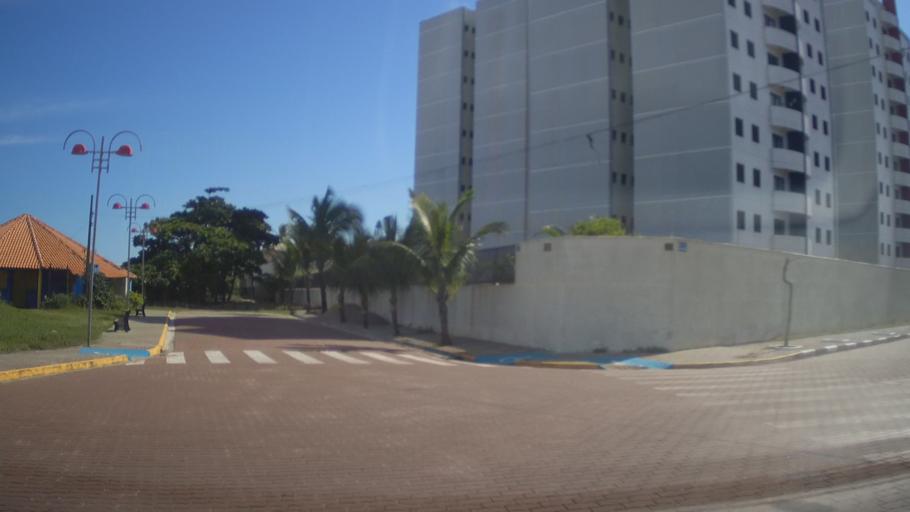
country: BR
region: Sao Paulo
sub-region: Itanhaem
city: Itanhaem
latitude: -24.1756
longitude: -46.7676
